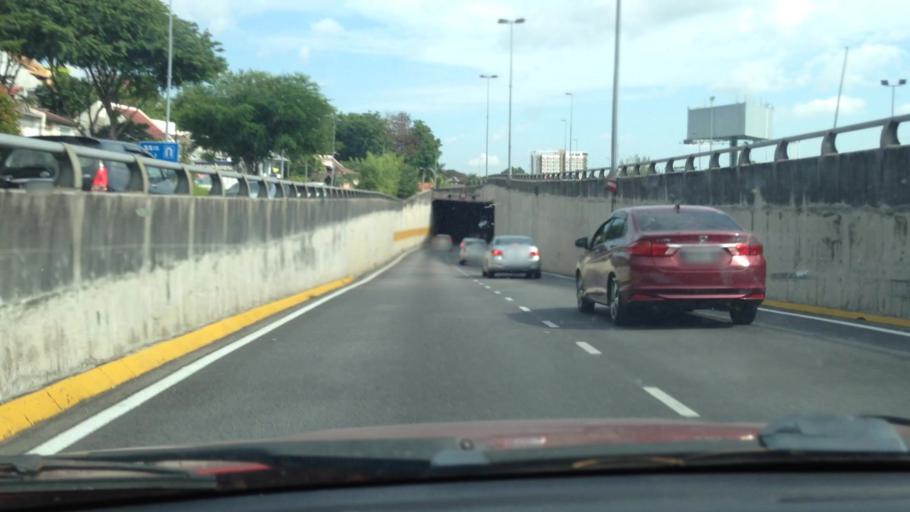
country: MY
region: Selangor
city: Subang Jaya
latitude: 3.0708
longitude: 101.5804
